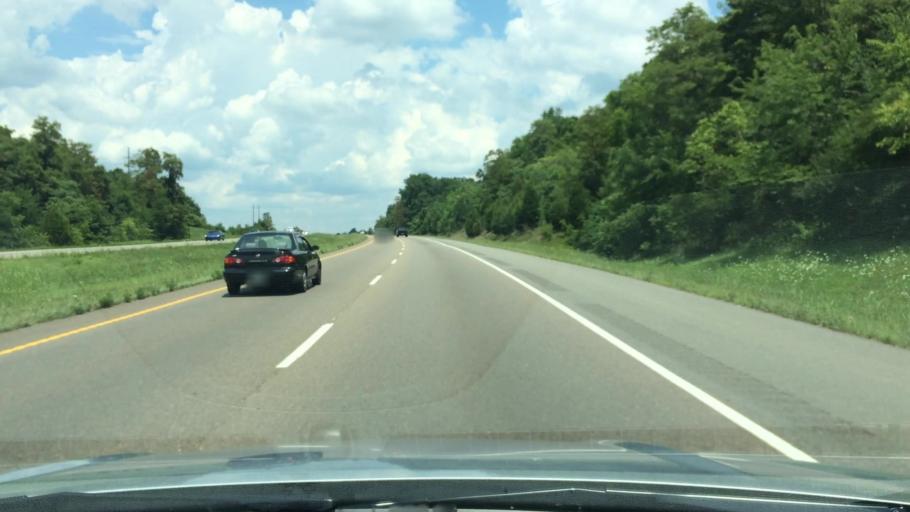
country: US
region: Tennessee
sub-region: Hamblen County
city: Morristown
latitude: 36.1835
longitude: -83.3160
